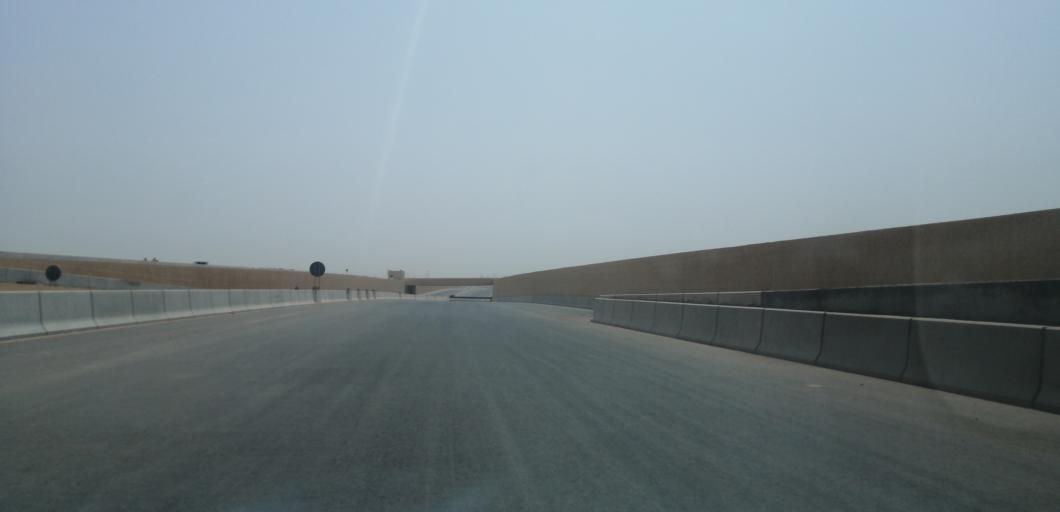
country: KW
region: Muhafazat al Jahra'
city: Al Jahra'
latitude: 29.4527
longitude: 47.5926
